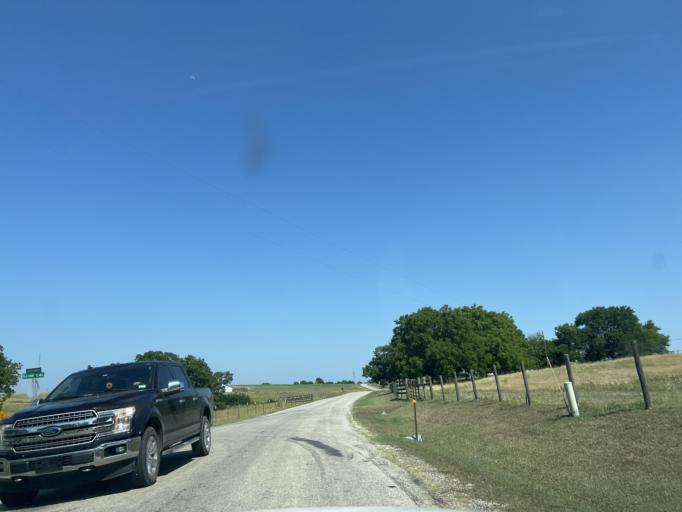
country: US
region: Texas
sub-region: Washington County
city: Brenham
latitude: 30.1706
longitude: -96.3357
